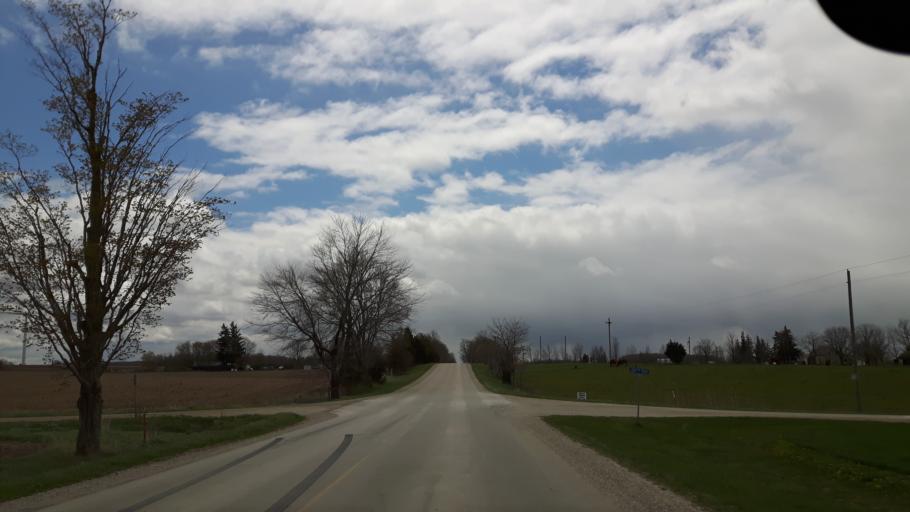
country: CA
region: Ontario
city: Bluewater
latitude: 43.4732
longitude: -81.6614
